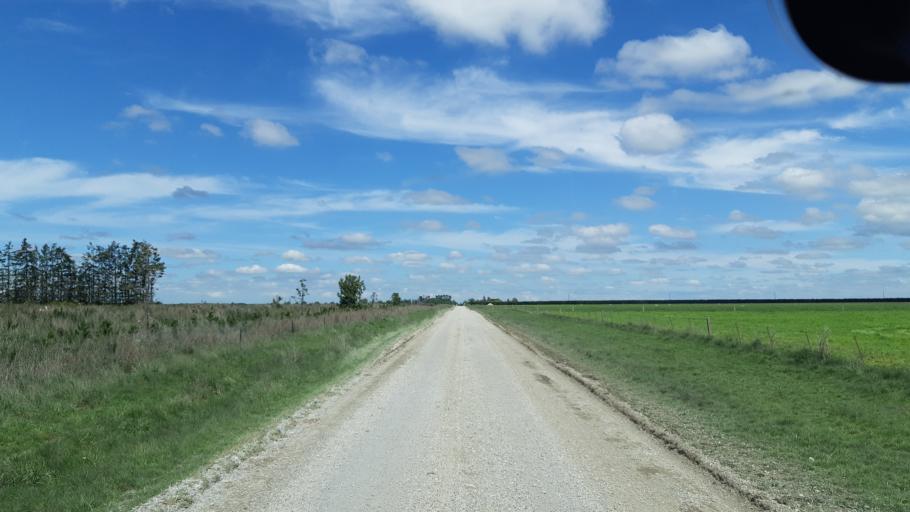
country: NZ
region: Canterbury
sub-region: Ashburton District
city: Methven
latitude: -43.7102
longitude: 171.4592
